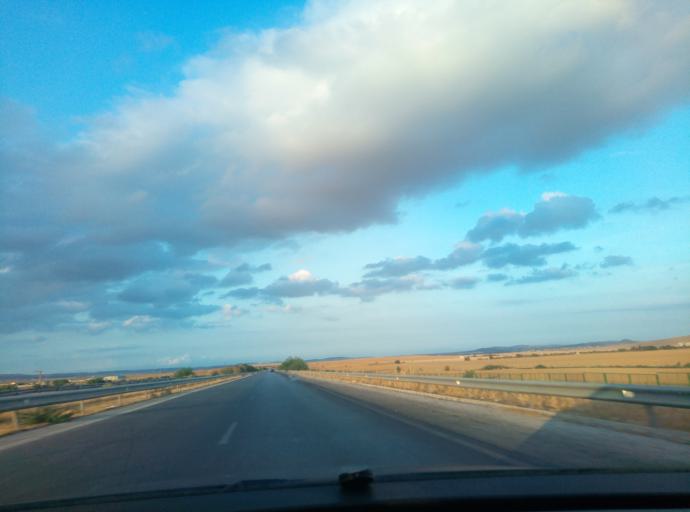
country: TN
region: Manouba
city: El Battan
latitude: 36.6941
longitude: 9.9362
